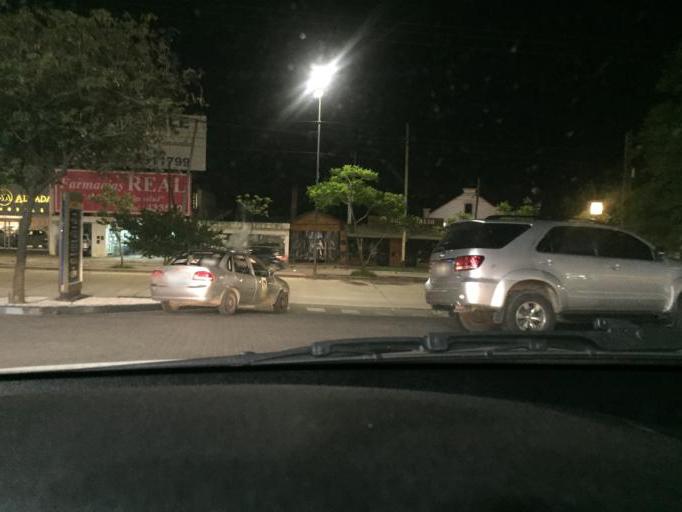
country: AR
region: Cordoba
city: Villa Allende
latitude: -31.2995
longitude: -64.2882
